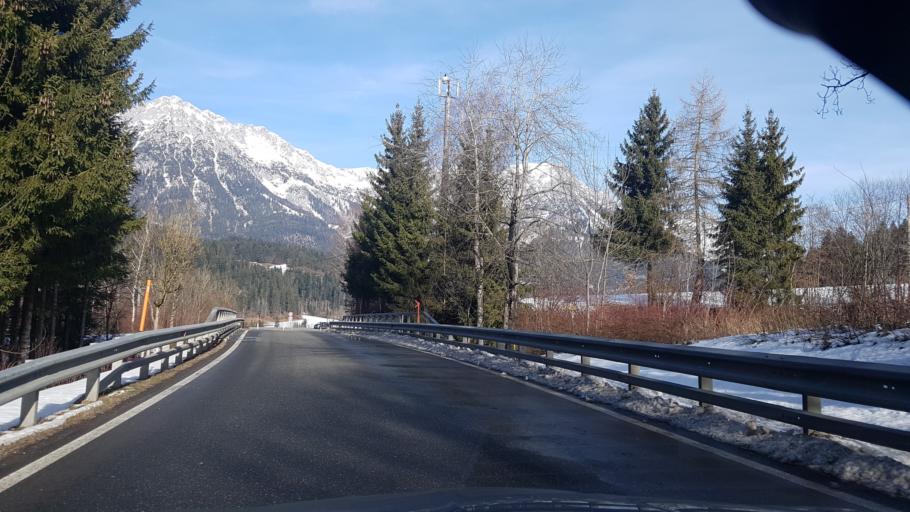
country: AT
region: Tyrol
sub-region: Politischer Bezirk Kufstein
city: Soll
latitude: 47.5129
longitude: 12.2172
